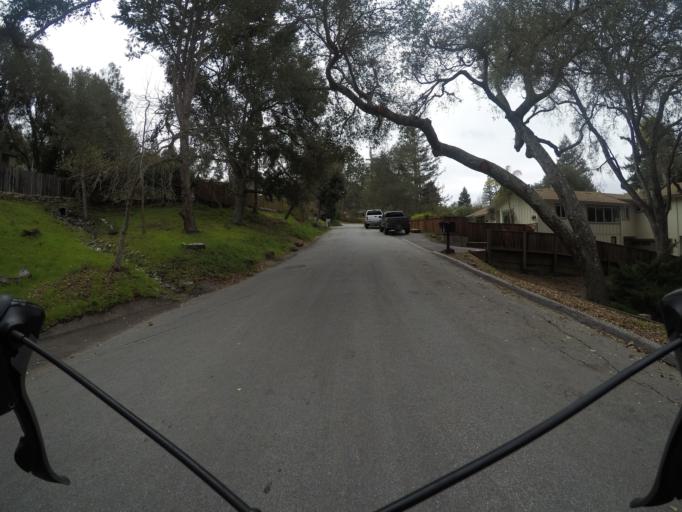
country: US
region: California
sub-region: Santa Cruz County
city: Scotts Valley
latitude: 37.0596
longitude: -121.9958
